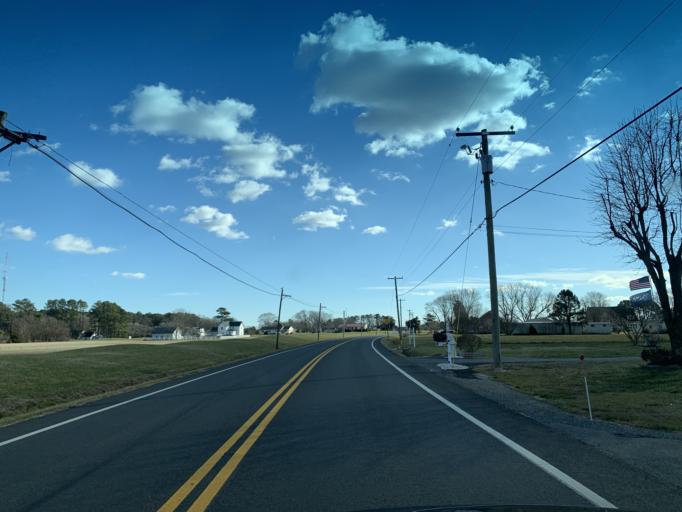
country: US
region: Maryland
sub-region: Worcester County
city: Berlin
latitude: 38.3510
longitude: -75.1935
